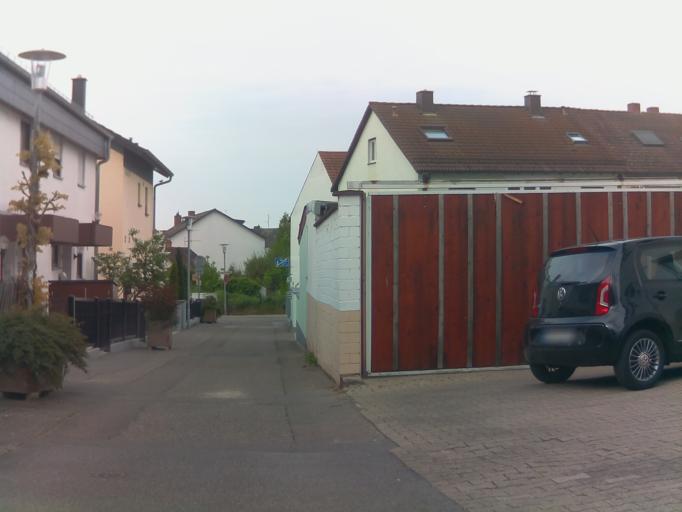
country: DE
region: Baden-Wuerttemberg
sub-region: Karlsruhe Region
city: Bruhl
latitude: 49.4063
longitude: 8.5536
